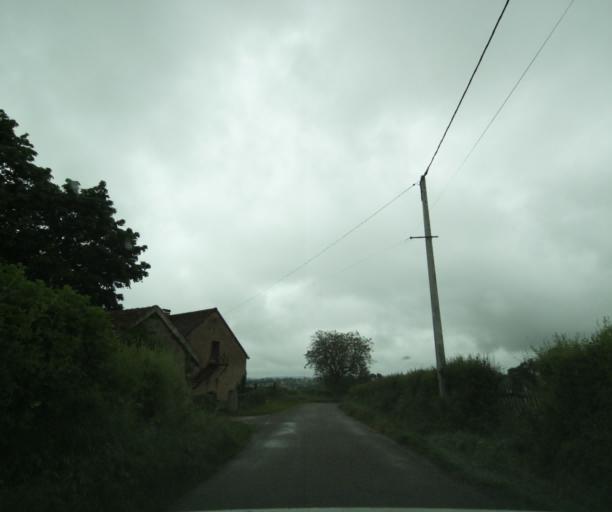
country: FR
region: Bourgogne
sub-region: Departement de Saone-et-Loire
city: Charolles
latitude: 46.4302
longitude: 4.3499
